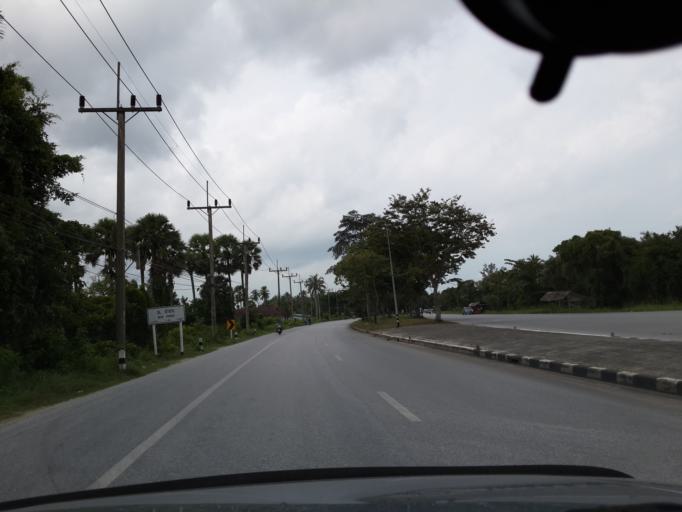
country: TH
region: Pattani
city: Yaring
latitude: 6.8679
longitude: 101.3247
